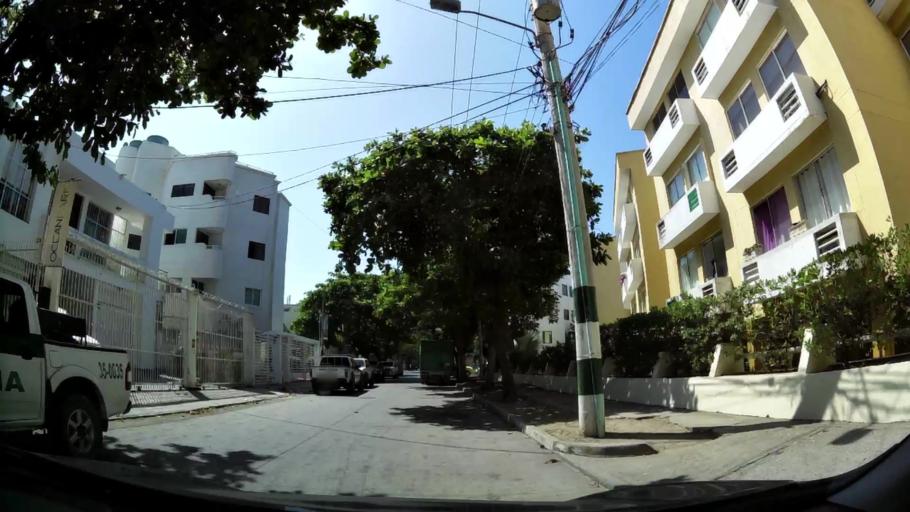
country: CO
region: Bolivar
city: Cartagena
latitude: 10.4474
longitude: -75.5194
